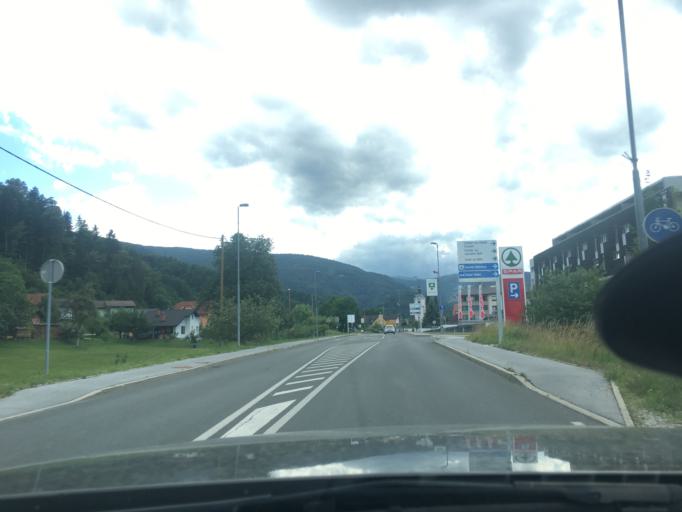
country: SI
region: Ruse
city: Ruse
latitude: 46.5412
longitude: 15.5202
